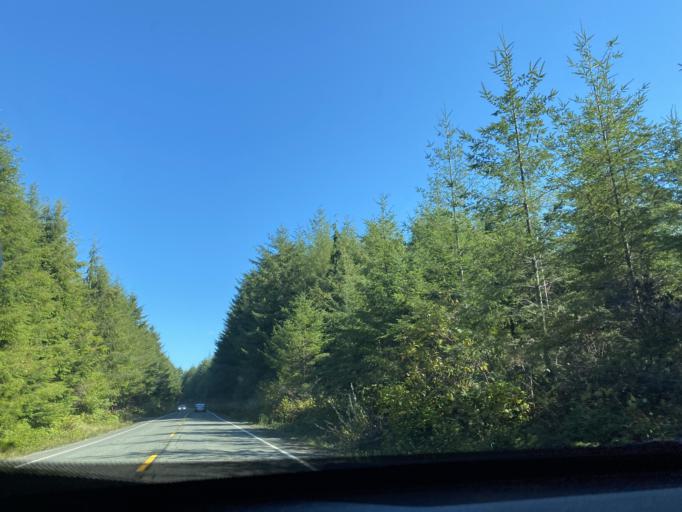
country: US
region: Washington
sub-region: Clallam County
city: Forks
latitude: 47.9222
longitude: -124.5030
